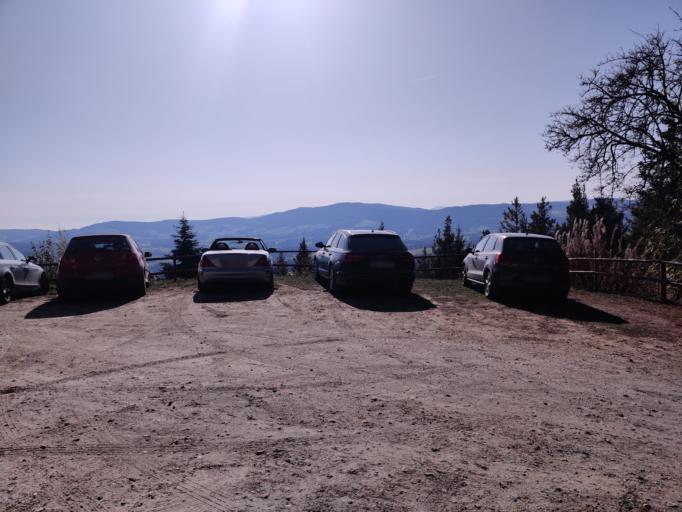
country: AT
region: Styria
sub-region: Politischer Bezirk Hartberg-Fuerstenfeld
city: Sankt Jakob im Walde
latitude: 47.4657
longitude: 15.8172
